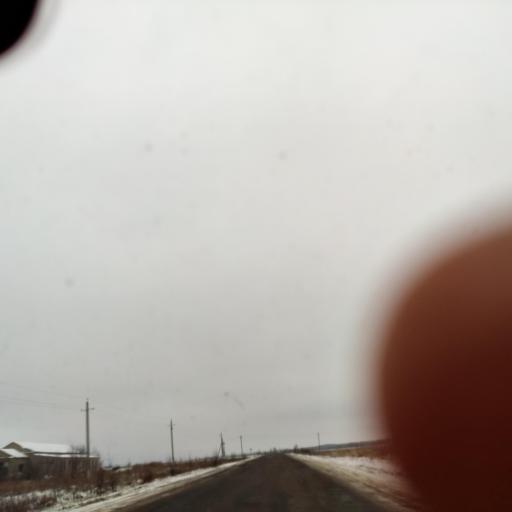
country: RU
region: Voronezj
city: Shilovo
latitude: 51.4434
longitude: 39.0268
